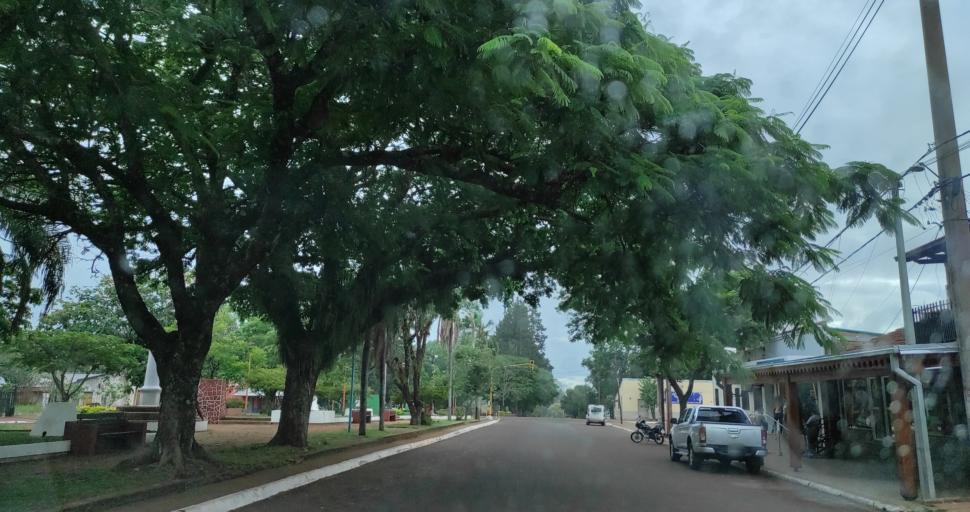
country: AR
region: Misiones
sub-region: Departamento de Apostoles
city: San Jose
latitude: -27.7683
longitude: -55.7781
